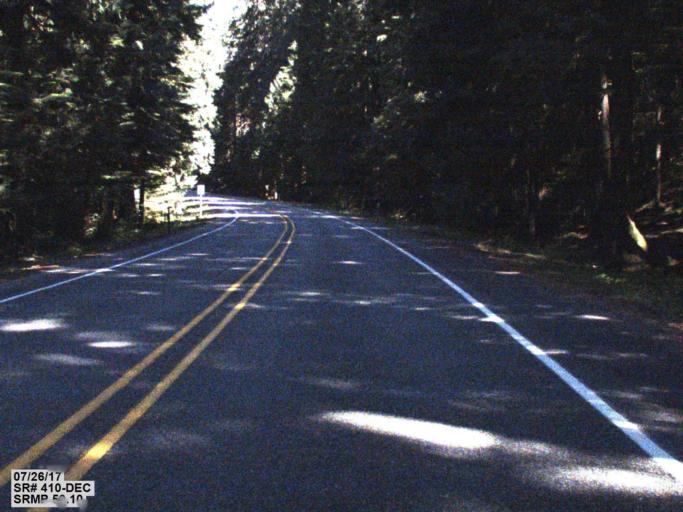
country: US
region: Washington
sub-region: King County
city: Riverbend
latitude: 47.0718
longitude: -121.5772
